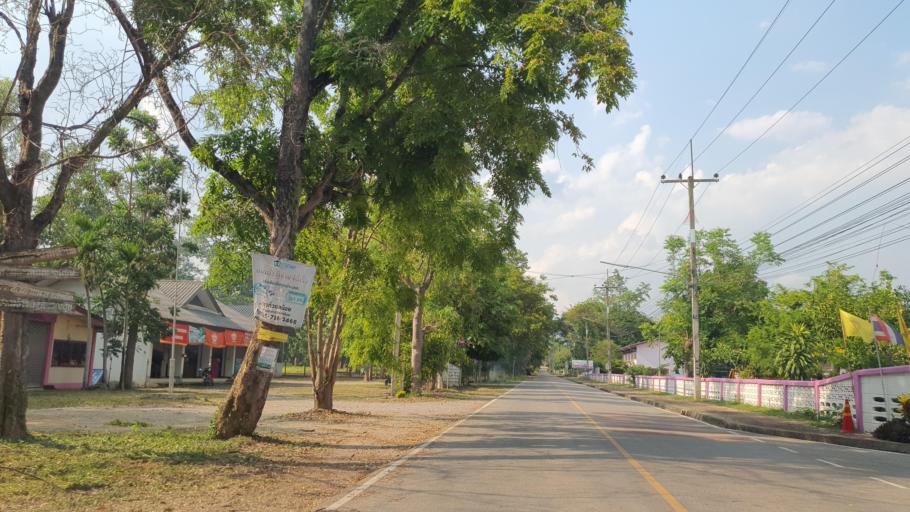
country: TH
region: Chiang Mai
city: San Pa Tong
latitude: 18.6438
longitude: 98.8473
